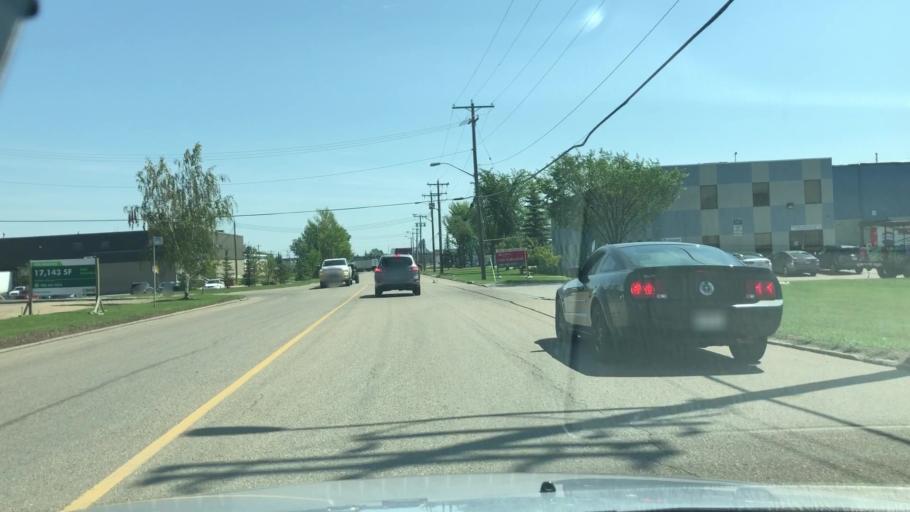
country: CA
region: Alberta
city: St. Albert
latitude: 53.5848
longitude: -113.5859
